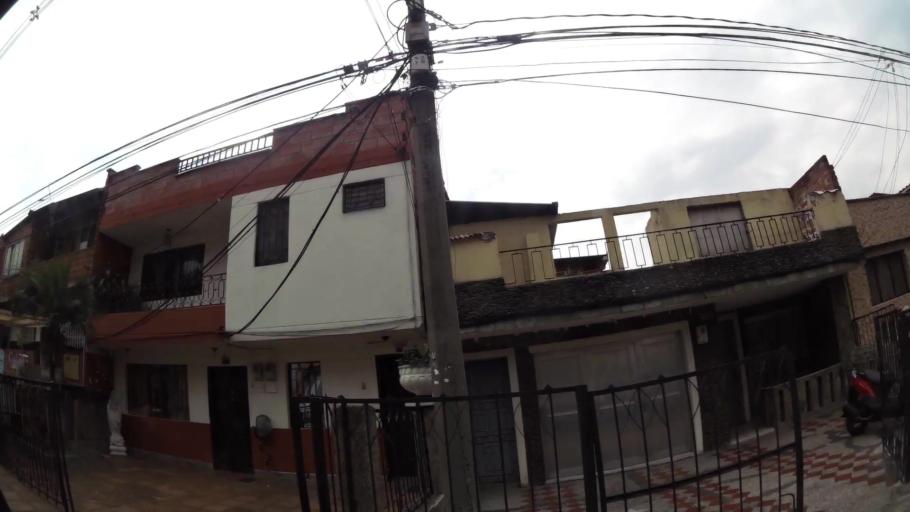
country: CO
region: Antioquia
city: Medellin
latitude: 6.2333
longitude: -75.5557
